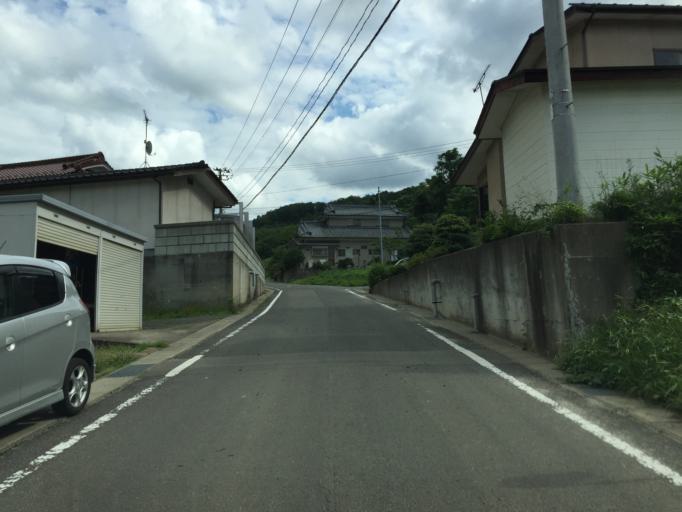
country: JP
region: Fukushima
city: Fukushima-shi
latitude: 37.7410
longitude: 140.4872
